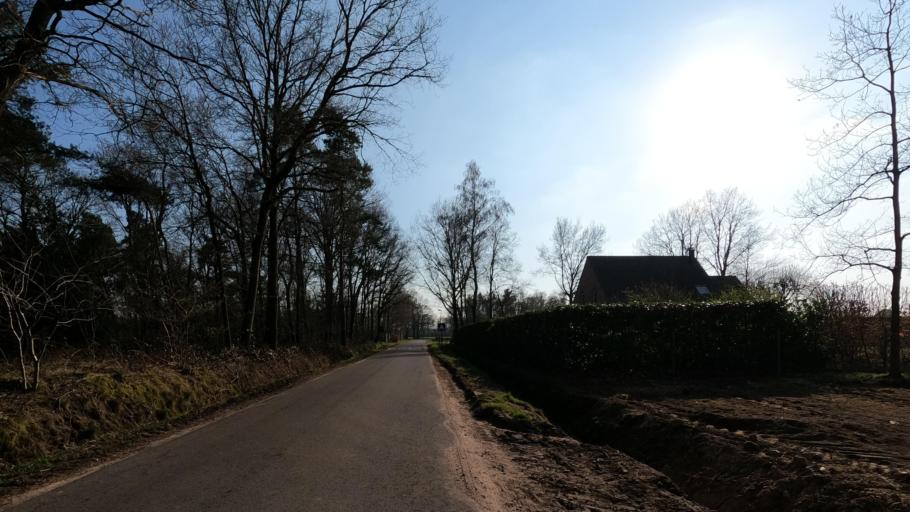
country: BE
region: Flanders
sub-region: Provincie Antwerpen
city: Merksplas
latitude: 51.3788
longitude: 4.8637
